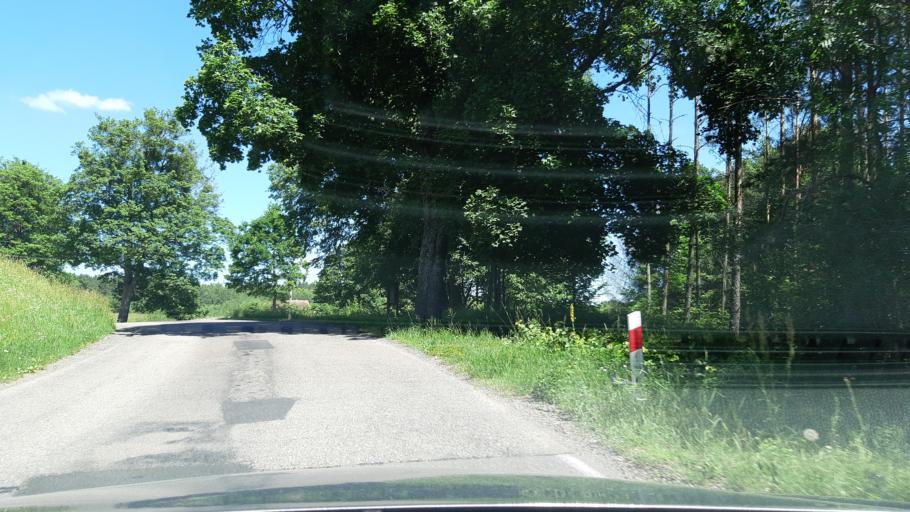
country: PL
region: Warmian-Masurian Voivodeship
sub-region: Powiat mragowski
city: Mikolajki
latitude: 53.7329
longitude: 21.5058
